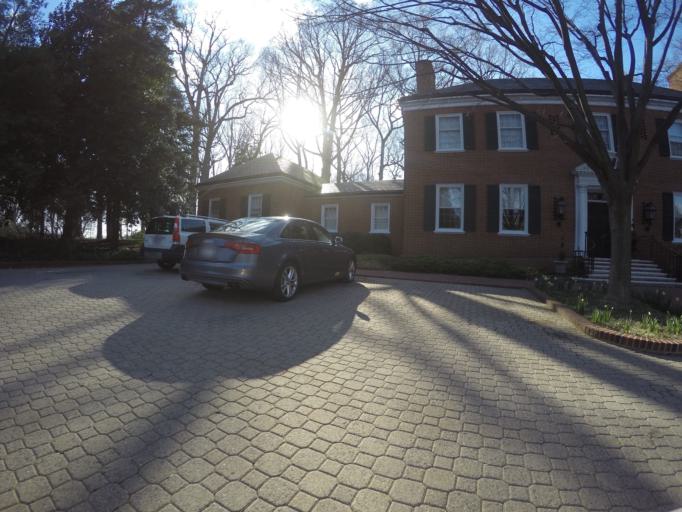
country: US
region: Maryland
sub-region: City of Baltimore
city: Baltimore
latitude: 39.3299
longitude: -76.6221
